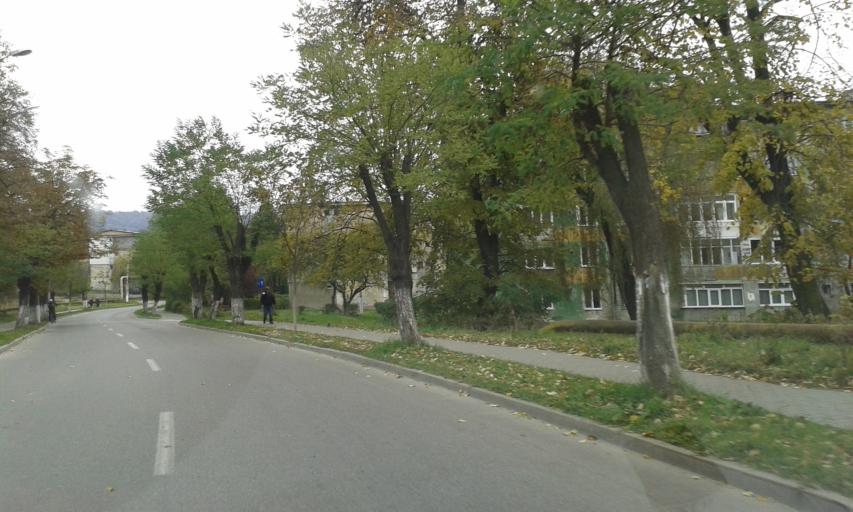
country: RO
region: Hunedoara
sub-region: Municipiul Petrosani
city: Petrosani
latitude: 45.4070
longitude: 23.3736
